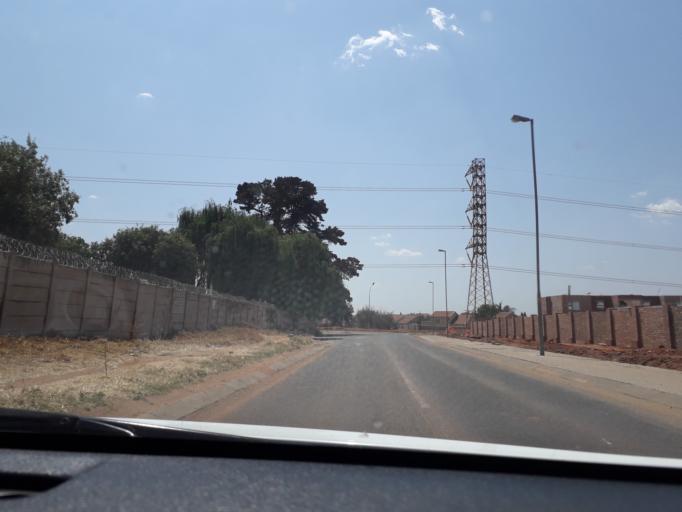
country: ZA
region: Gauteng
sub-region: City of Johannesburg Metropolitan Municipality
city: Modderfontein
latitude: -26.0768
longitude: 28.1982
